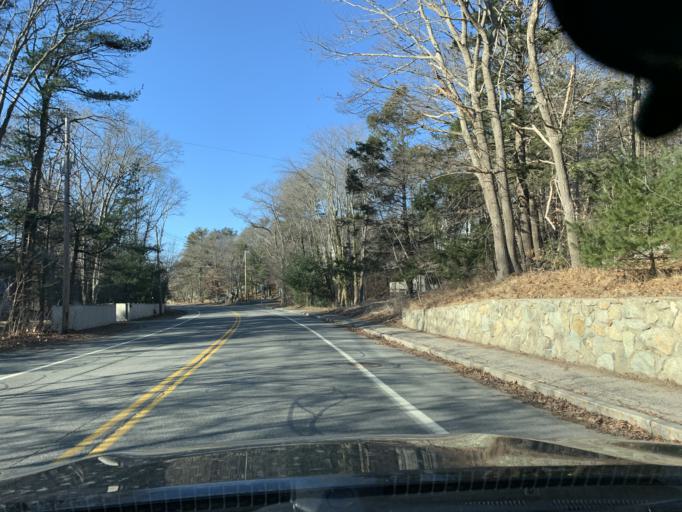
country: US
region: Massachusetts
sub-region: Essex County
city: Essex
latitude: 42.5873
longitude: -70.7834
